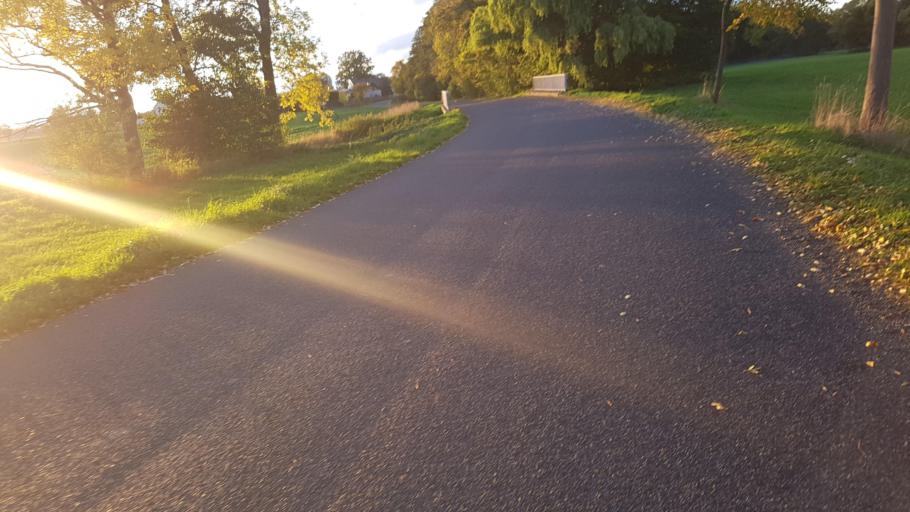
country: DE
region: Saxony
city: Priestewitz
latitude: 51.2317
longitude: 13.5404
